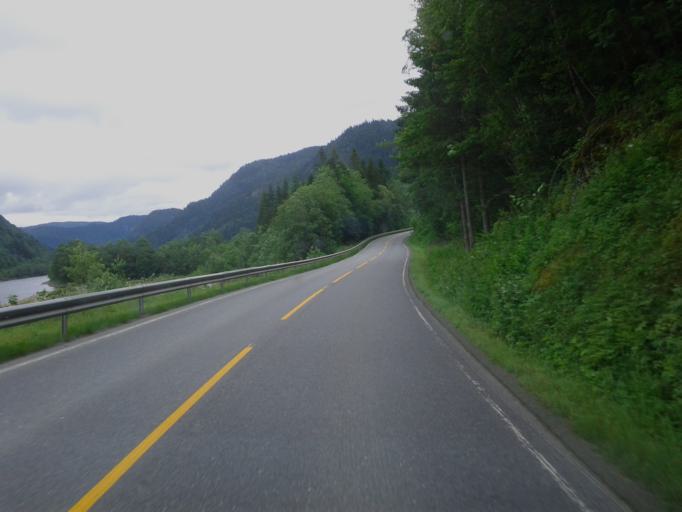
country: NO
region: Sor-Trondelag
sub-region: Midtre Gauldal
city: Storen
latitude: 63.0160
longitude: 10.3455
